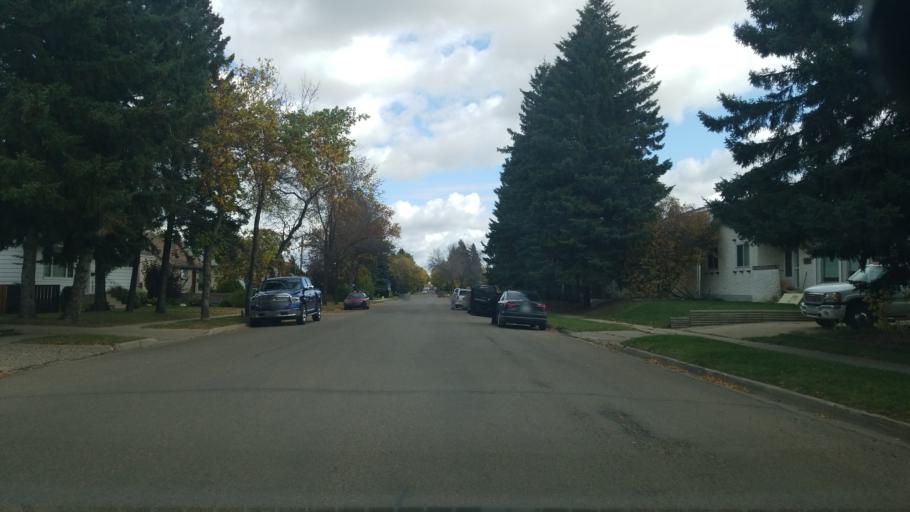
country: CA
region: Saskatchewan
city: Lloydminster
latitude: 53.2807
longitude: -110.0198
